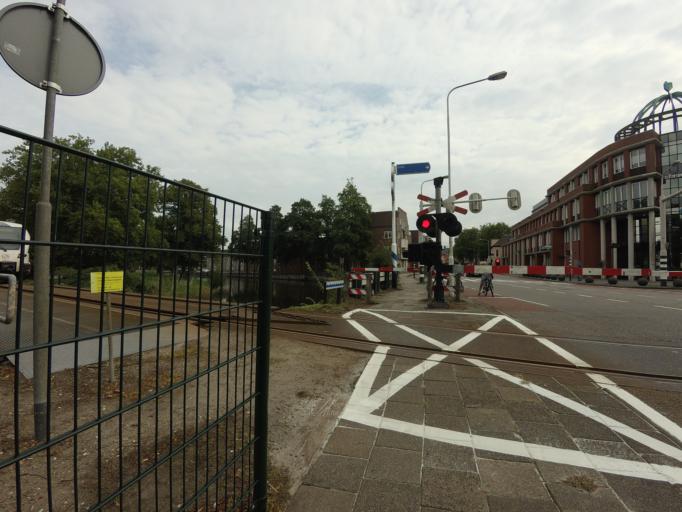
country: NL
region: Friesland
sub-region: Sudwest Fryslan
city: Sneek
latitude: 53.0347
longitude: 5.6559
